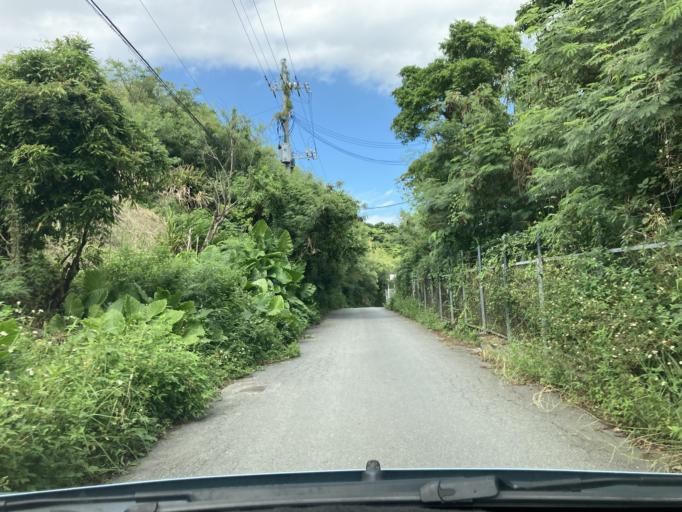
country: JP
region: Okinawa
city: Ginowan
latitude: 26.2763
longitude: 127.7805
